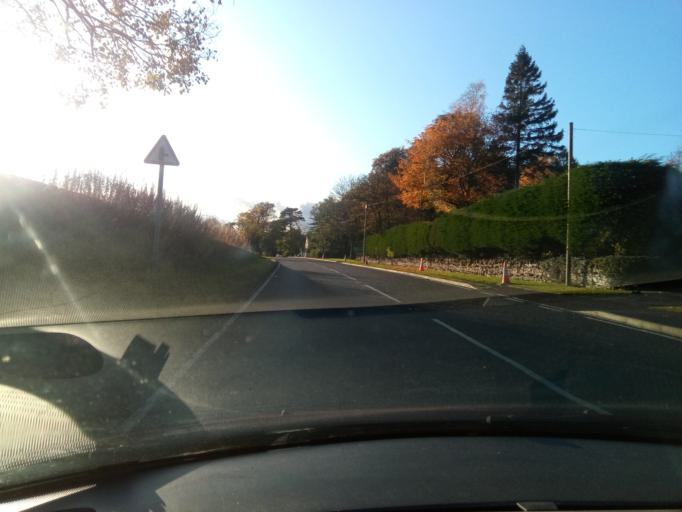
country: GB
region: England
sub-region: County Durham
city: Stanhope
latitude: 54.7496
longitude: -2.0255
